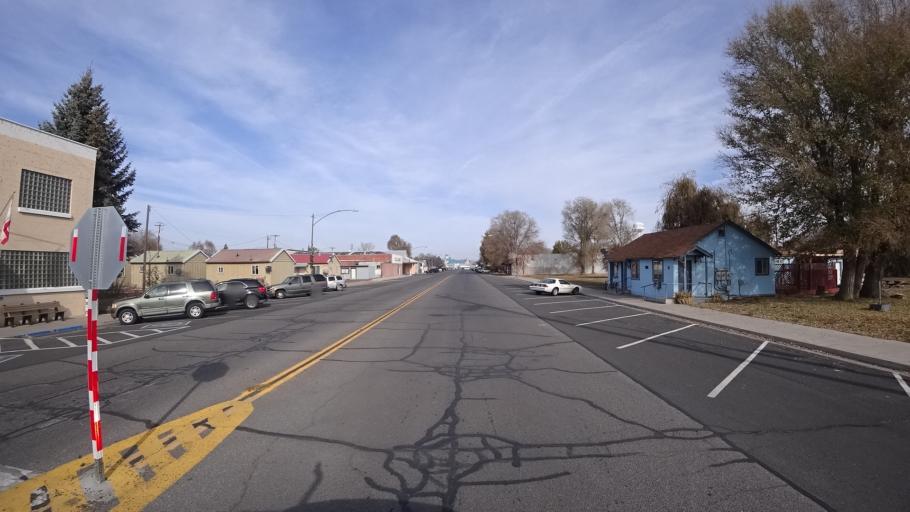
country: US
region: California
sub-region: Siskiyou County
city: Tulelake
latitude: 41.9538
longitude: -121.4767
